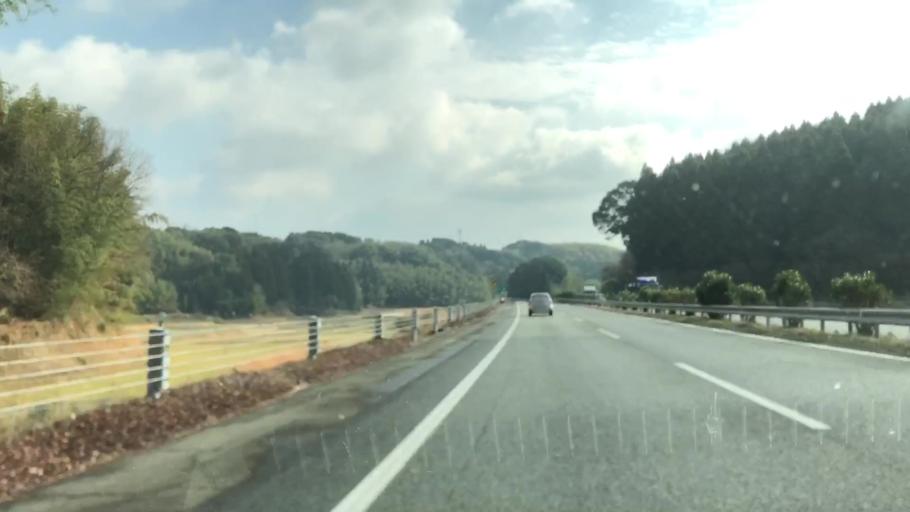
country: JP
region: Kumamoto
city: Yamaga
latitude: 33.0308
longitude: 130.5743
